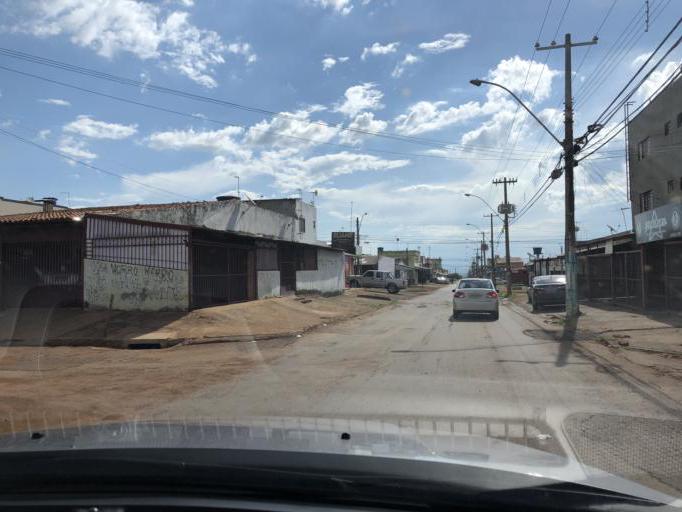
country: BR
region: Federal District
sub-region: Brasilia
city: Brasilia
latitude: -15.7943
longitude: -48.1229
